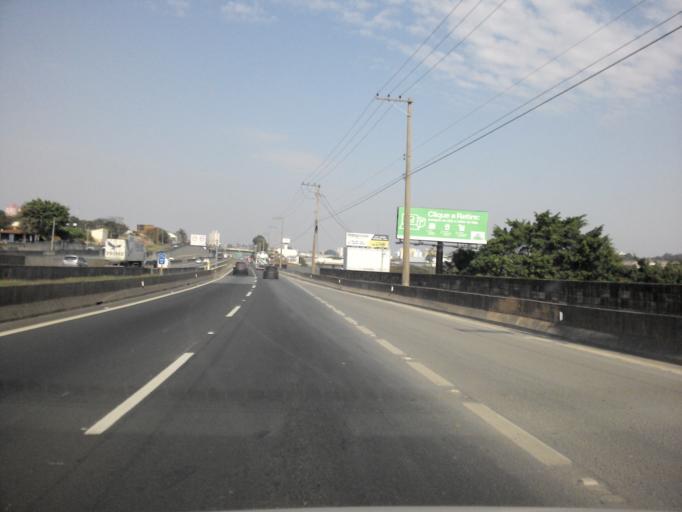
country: BR
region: Sao Paulo
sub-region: Campinas
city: Campinas
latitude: -22.9042
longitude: -47.1080
